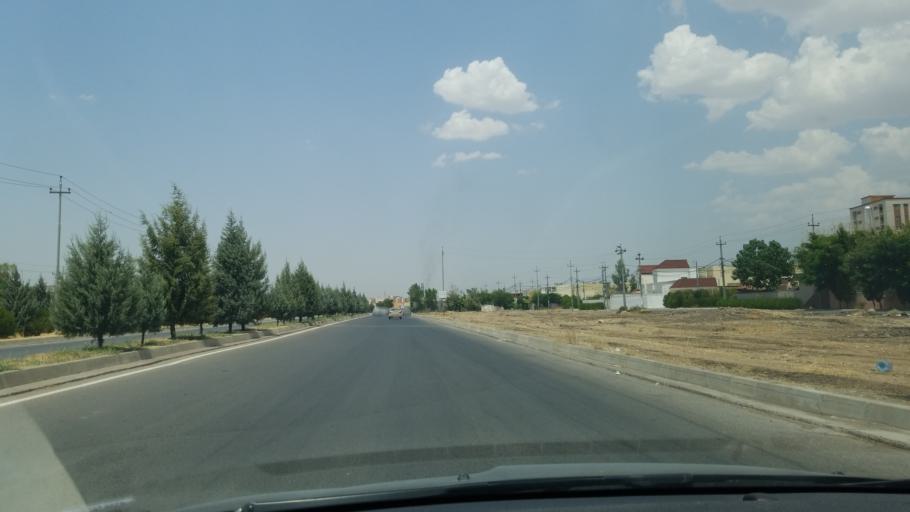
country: IQ
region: Arbil
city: Erbil
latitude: 36.1678
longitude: 44.0588
